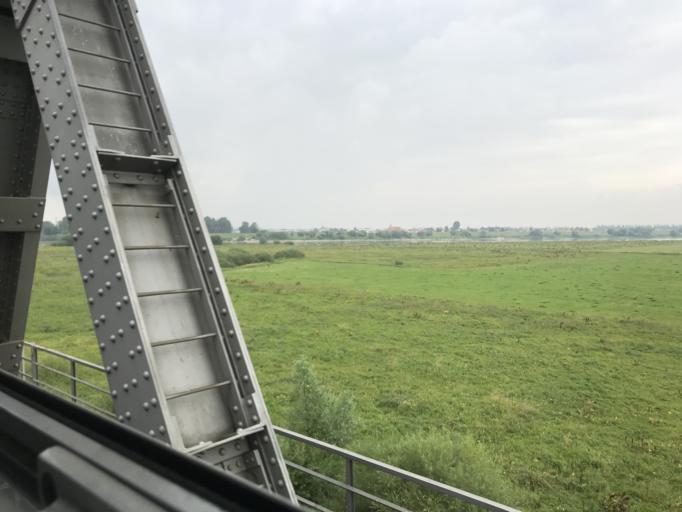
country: PL
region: Pomeranian Voivodeship
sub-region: Powiat malborski
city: Lisewo Malborskie
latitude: 54.0931
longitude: 18.8154
